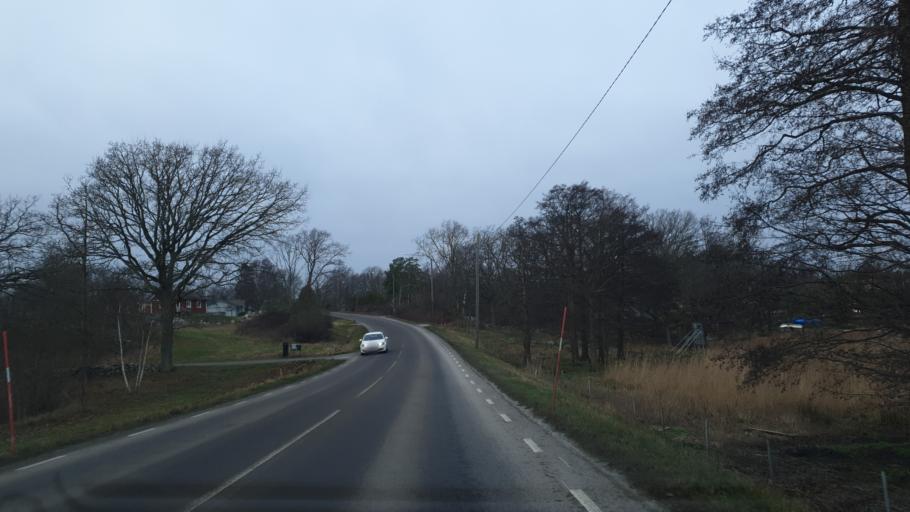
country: SE
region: Blekinge
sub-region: Karlskrona Kommun
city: Sturko
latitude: 56.1112
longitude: 15.7071
